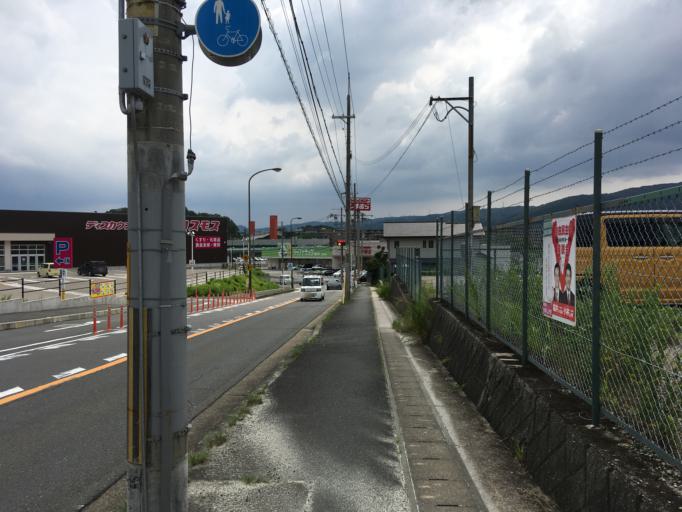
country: JP
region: Nara
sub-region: Ikoma-shi
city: Ikoma
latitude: 34.6710
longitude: 135.7178
